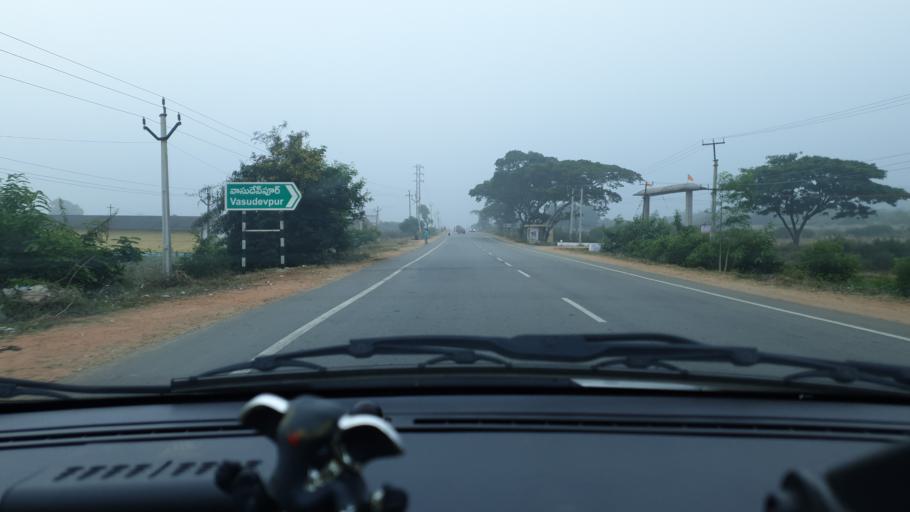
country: IN
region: Telangana
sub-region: Mahbubnagar
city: Farrukhnagar
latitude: 16.9229
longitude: 78.5272
